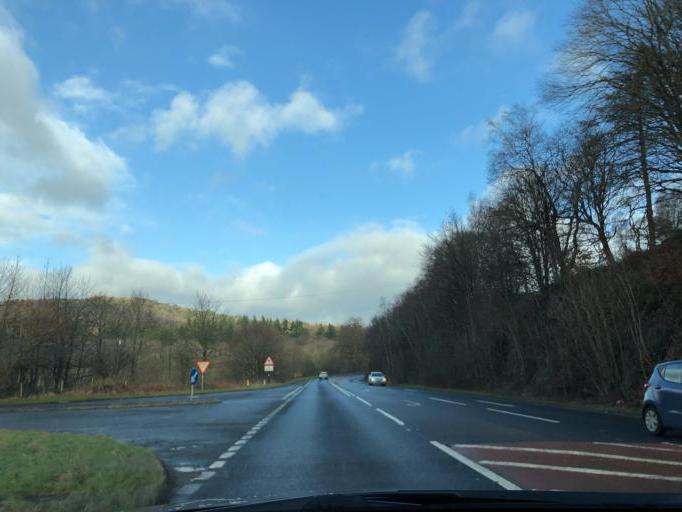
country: GB
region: England
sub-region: Cumbria
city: Grange-over-Sands
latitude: 54.2599
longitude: -2.9883
